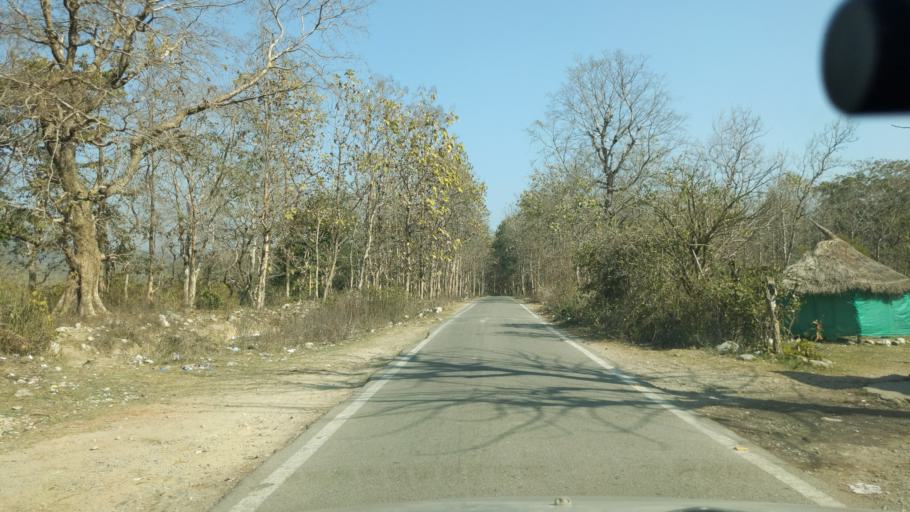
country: IN
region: Uttarakhand
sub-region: Naini Tal
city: Ramnagar
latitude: 29.4232
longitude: 79.1388
